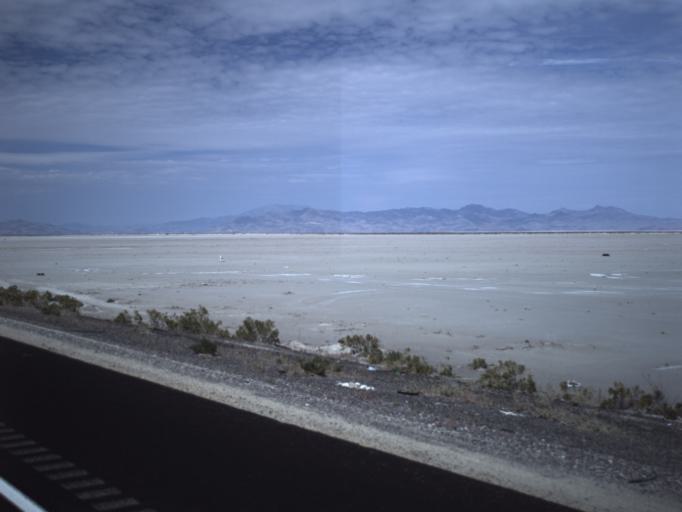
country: US
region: Utah
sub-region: Tooele County
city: Wendover
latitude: 40.7322
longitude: -113.5175
